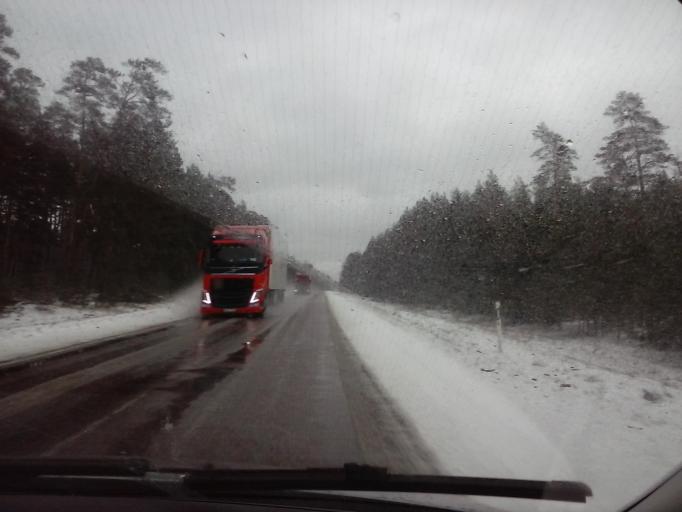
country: LV
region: Strenci
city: Seda
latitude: 57.6269
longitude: 25.7984
